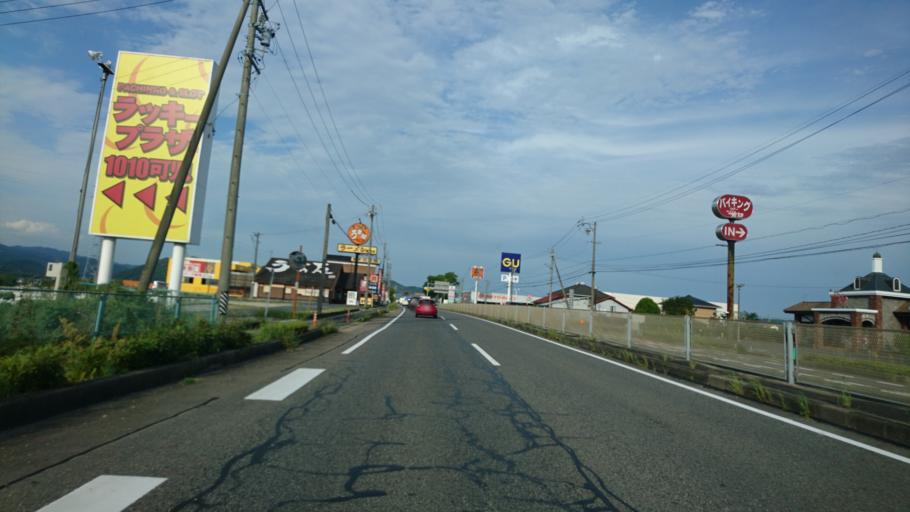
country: JP
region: Gifu
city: Minokamo
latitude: 35.4350
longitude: 137.0631
